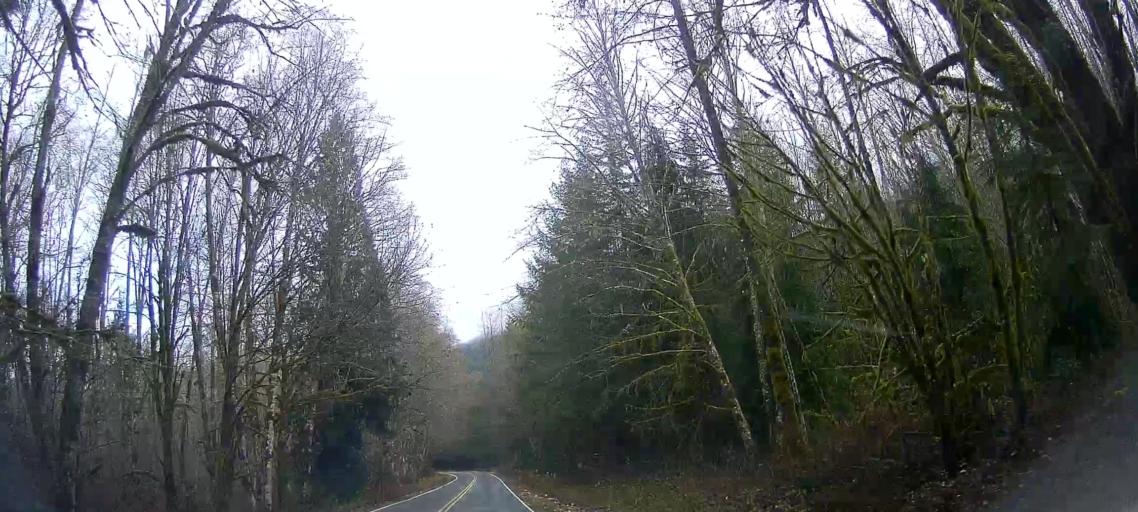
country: US
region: Washington
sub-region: Snohomish County
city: Darrington
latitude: 48.4891
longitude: -121.4797
